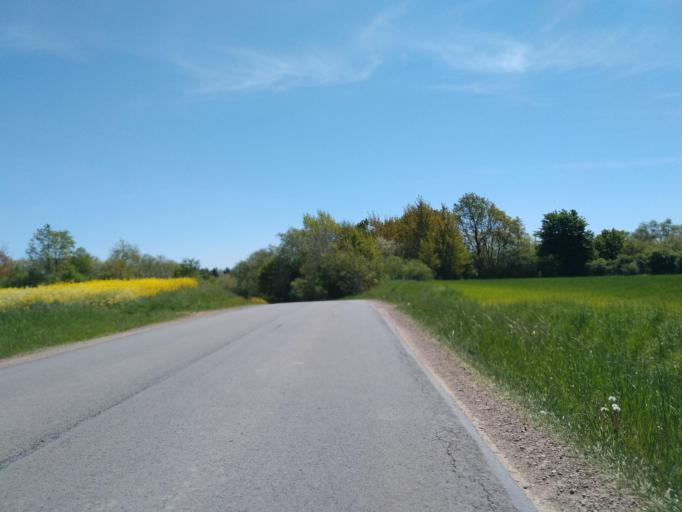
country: PL
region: Subcarpathian Voivodeship
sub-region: Powiat krosnienski
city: Sieniawa
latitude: 49.5453
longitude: 21.9493
